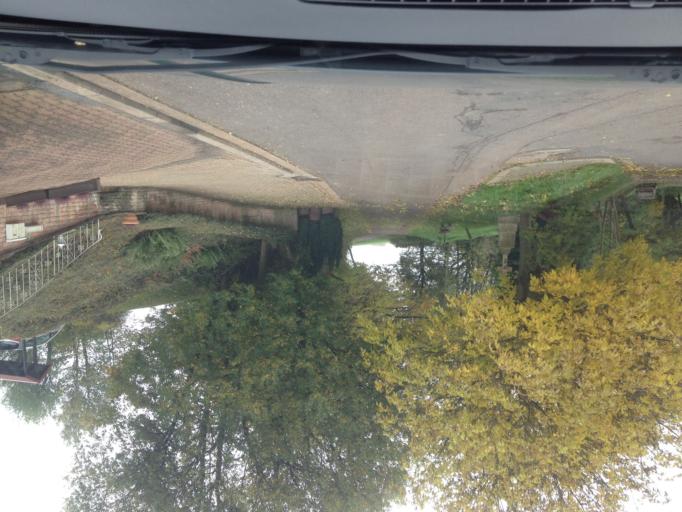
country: DE
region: Saarland
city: Eppelborn
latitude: 49.4397
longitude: 6.9646
